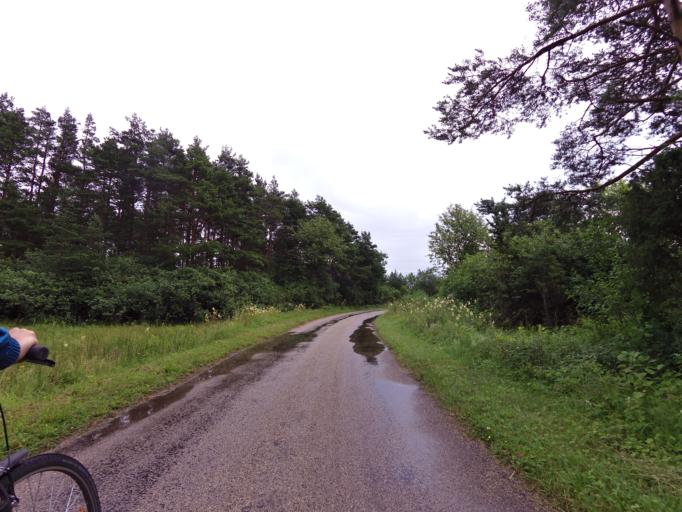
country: EE
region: Laeaene
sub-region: Vormsi vald
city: Hullo
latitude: 59.0208
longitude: 23.2993
